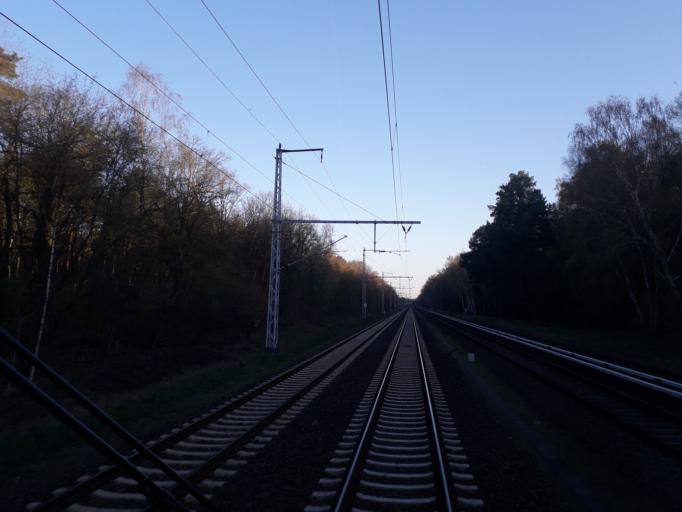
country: DE
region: Brandenburg
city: Zeuthen
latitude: 52.3805
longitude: 13.6092
